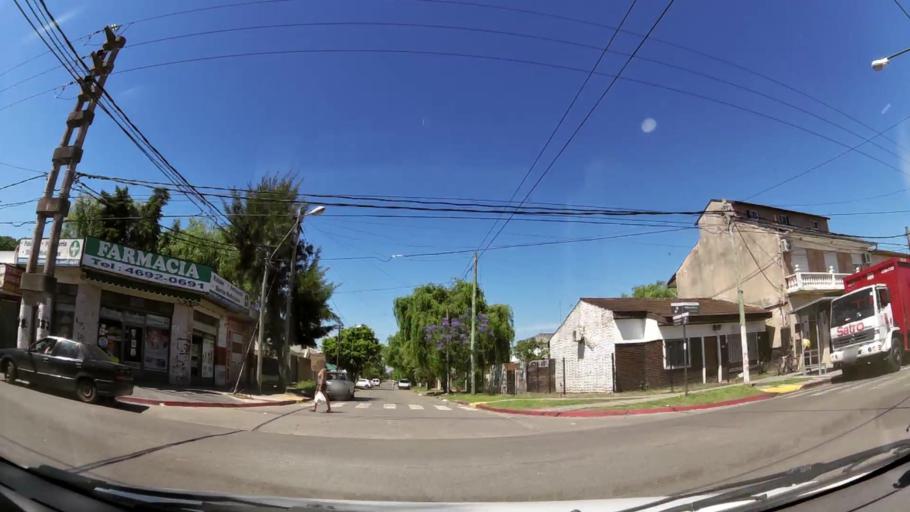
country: AR
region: Buenos Aires
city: Ituzaingo
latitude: -34.6841
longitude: -58.6575
